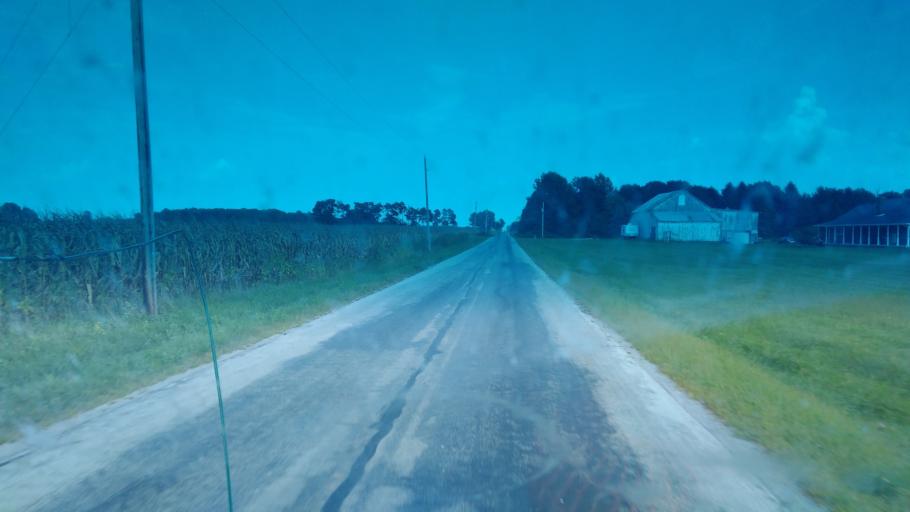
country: US
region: Ohio
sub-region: Hardin County
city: Forest
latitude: 40.9049
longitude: -83.4860
